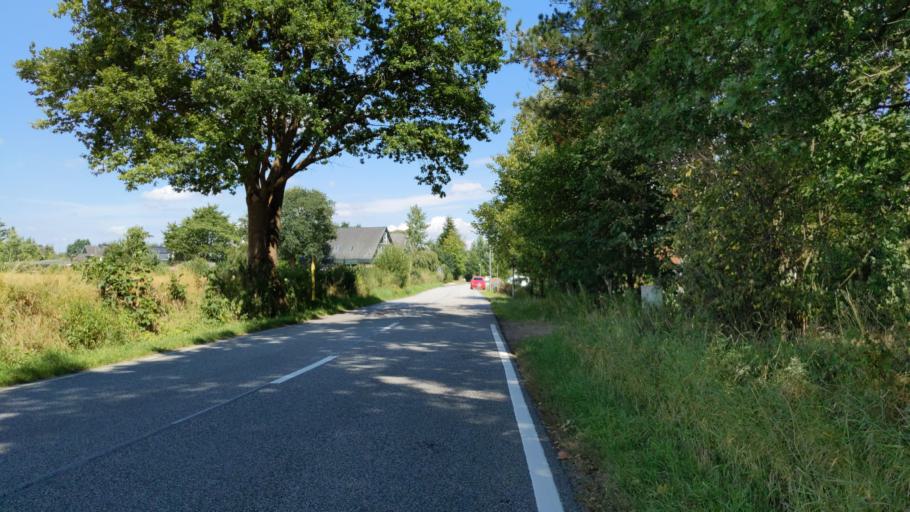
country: DE
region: Schleswig-Holstein
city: Krummesse
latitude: 53.8065
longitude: 10.6848
